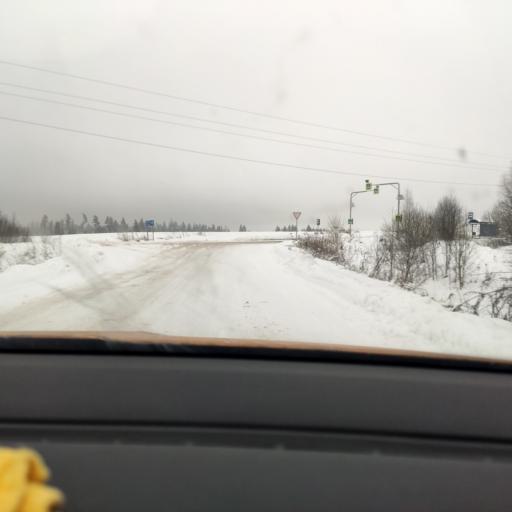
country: RU
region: Moskovskaya
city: Yershovo
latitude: 55.7876
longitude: 36.7858
